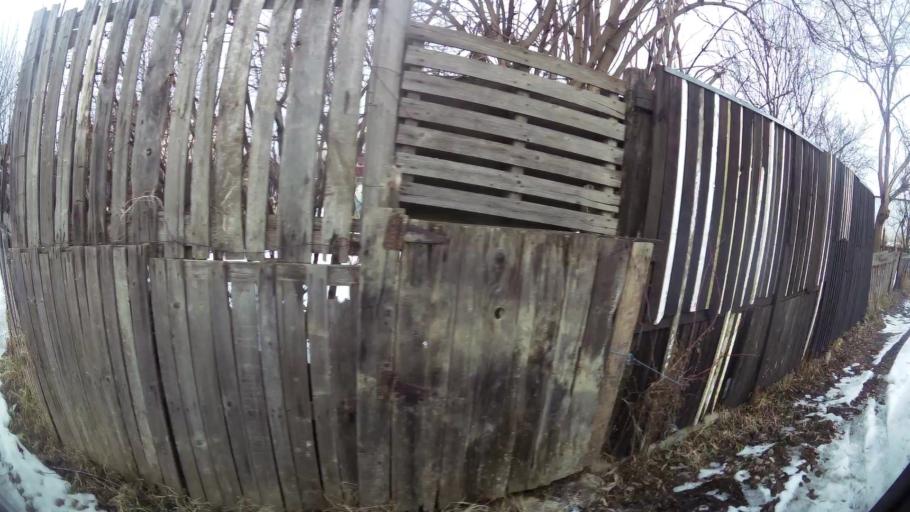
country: RO
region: Ilfov
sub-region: Comuna Popesti-Leordeni
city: Popesti-Leordeni
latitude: 44.4011
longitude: 26.1793
